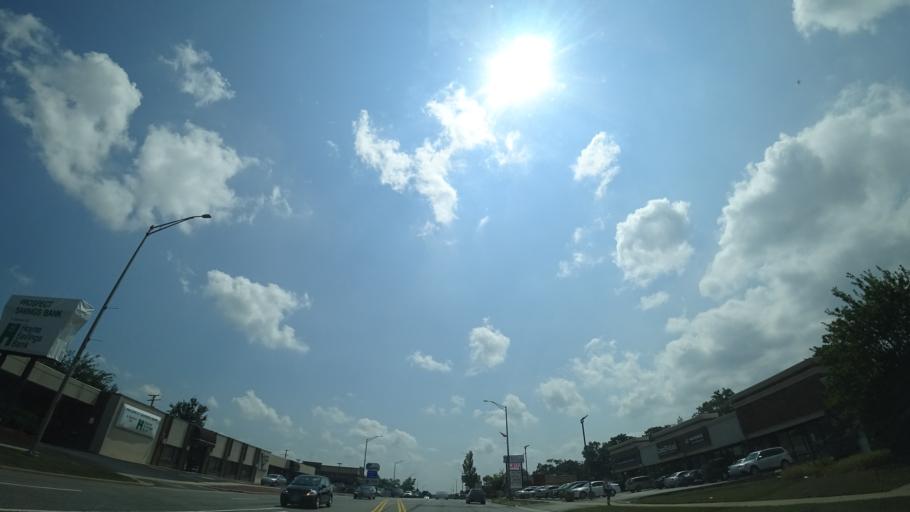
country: US
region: Illinois
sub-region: Cook County
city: Worth
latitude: 41.6887
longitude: -87.7975
